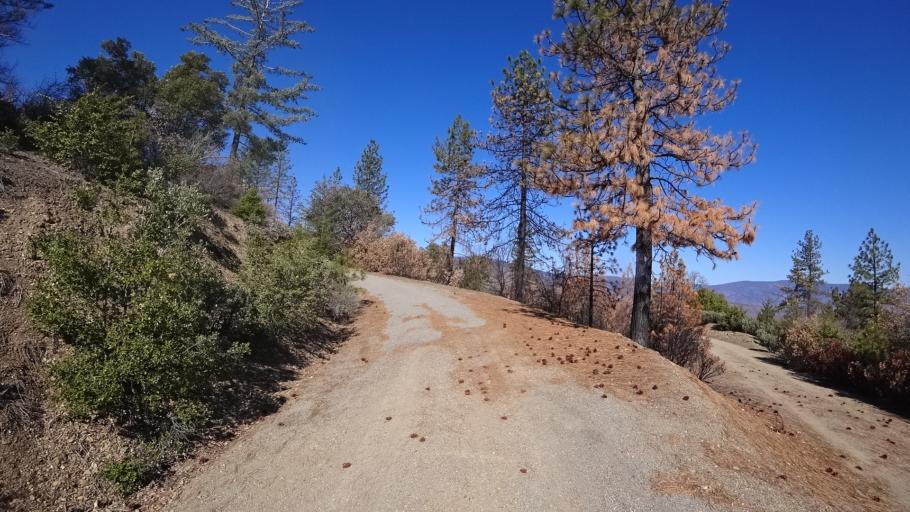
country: US
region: California
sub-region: Tehama County
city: Rancho Tehama Reserve
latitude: 39.6793
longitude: -122.7079
